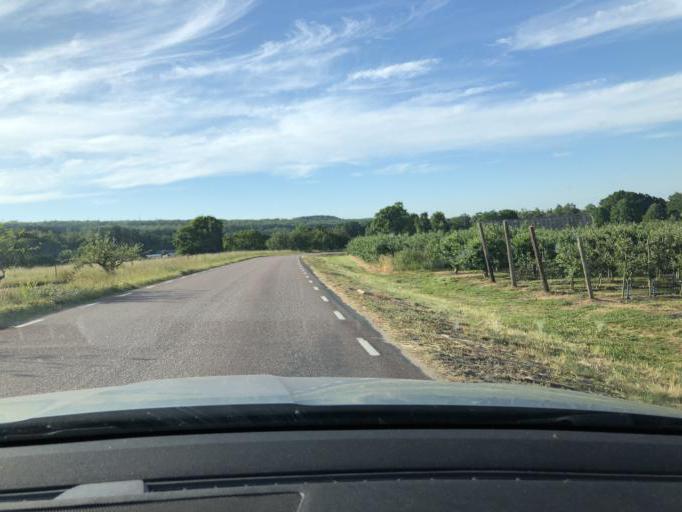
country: SE
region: Blekinge
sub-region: Solvesborgs Kommun
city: Soelvesborg
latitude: 56.1550
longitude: 14.6013
